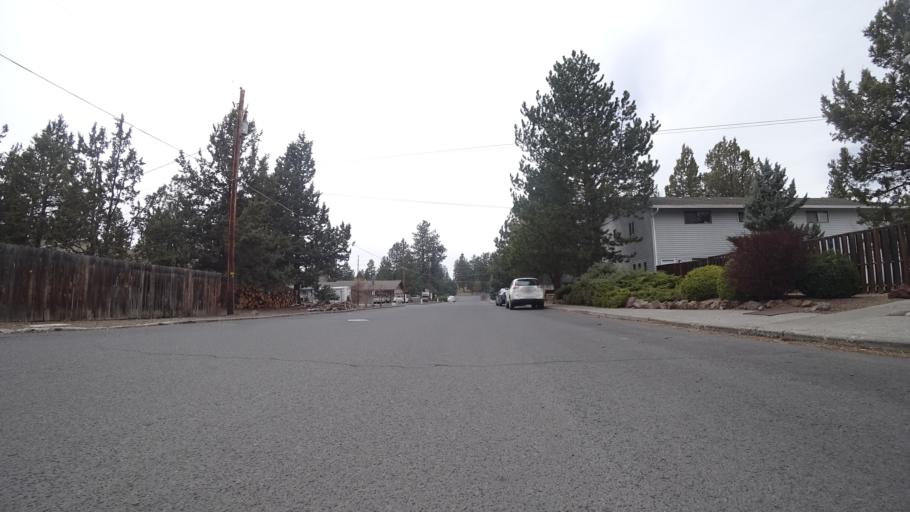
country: US
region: Oregon
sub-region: Deschutes County
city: Bend
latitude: 44.0460
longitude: -121.2815
